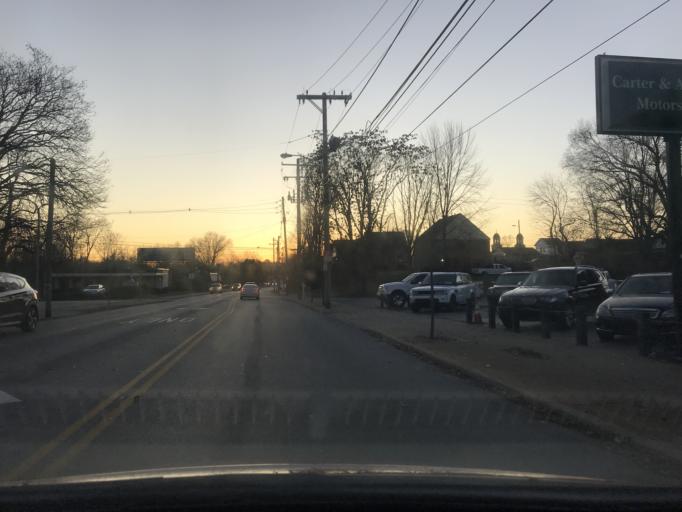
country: US
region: Kentucky
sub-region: Jefferson County
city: Audubon Park
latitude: 38.2357
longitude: -85.7279
